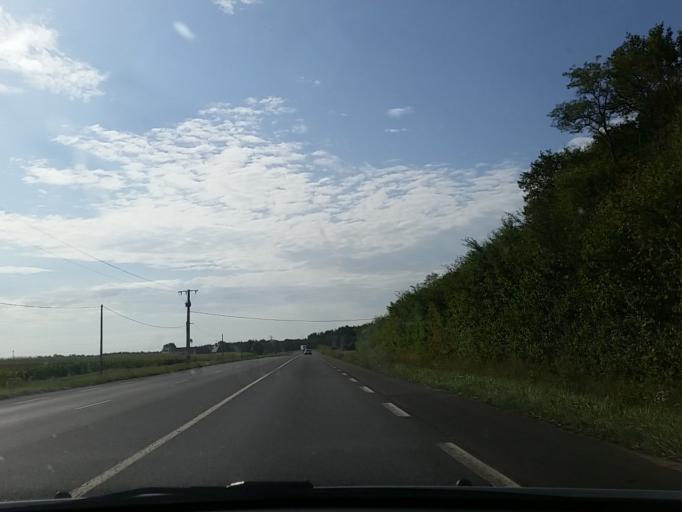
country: FR
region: Centre
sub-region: Departement du Loir-et-Cher
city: Soings-en-Sologne
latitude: 47.4442
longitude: 1.5425
